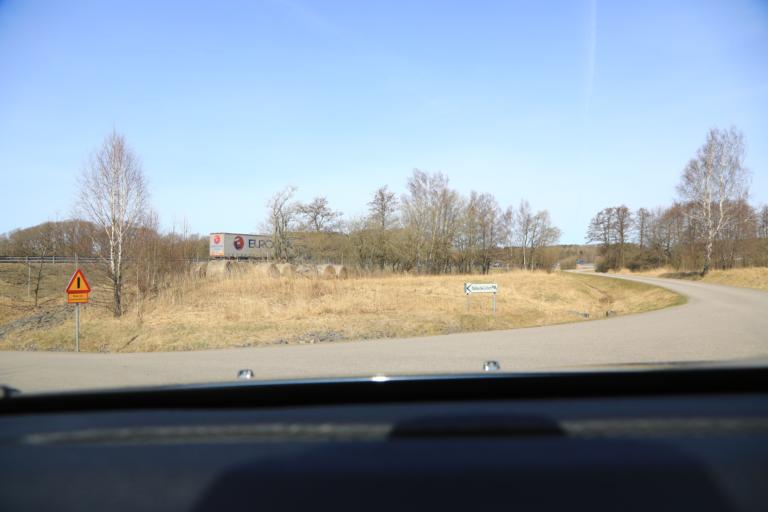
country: SE
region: Halland
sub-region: Kungsbacka Kommun
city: Frillesas
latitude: 57.2602
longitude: 12.2172
